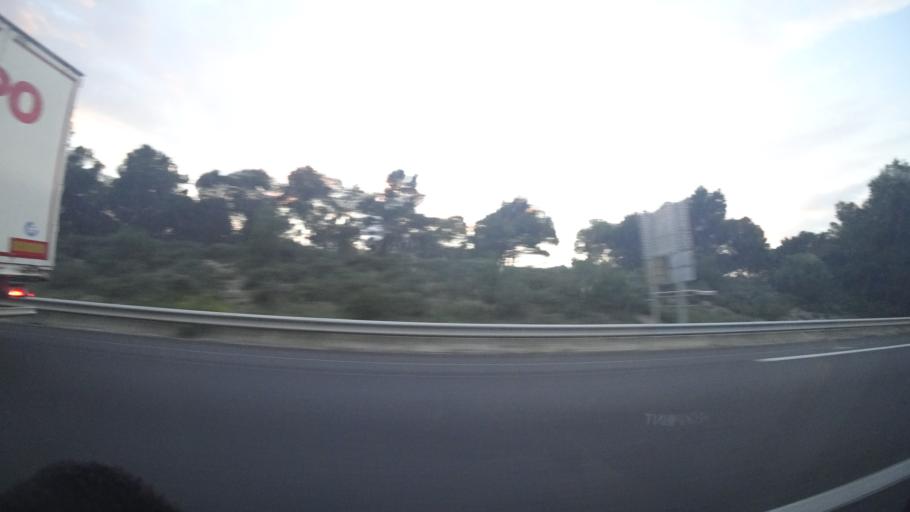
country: FR
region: Languedoc-Roussillon
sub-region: Departement de l'Aude
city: Peyriac-de-Mer
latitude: 43.1252
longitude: 2.9603
